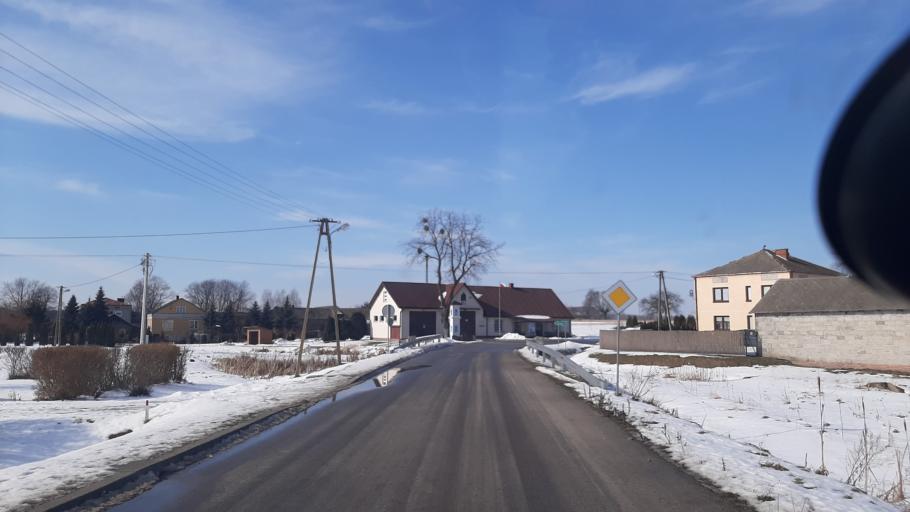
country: PL
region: Lublin Voivodeship
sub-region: Powiat pulawski
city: Baranow
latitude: 51.5384
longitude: 22.1496
